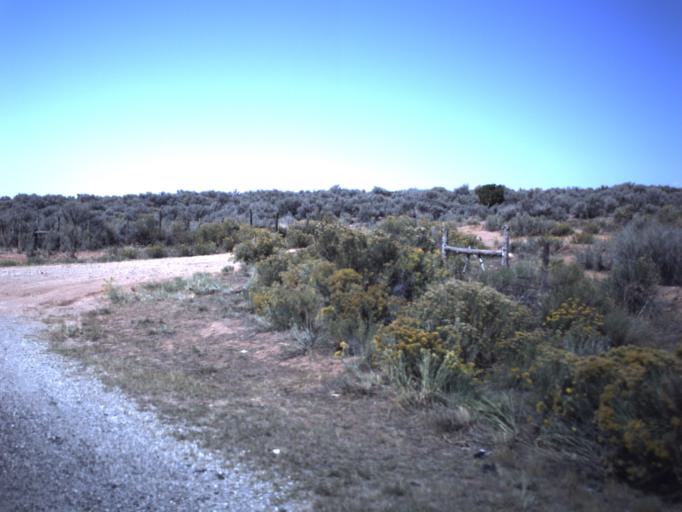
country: US
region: Utah
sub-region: Grand County
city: Moab
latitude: 38.3168
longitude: -109.3141
